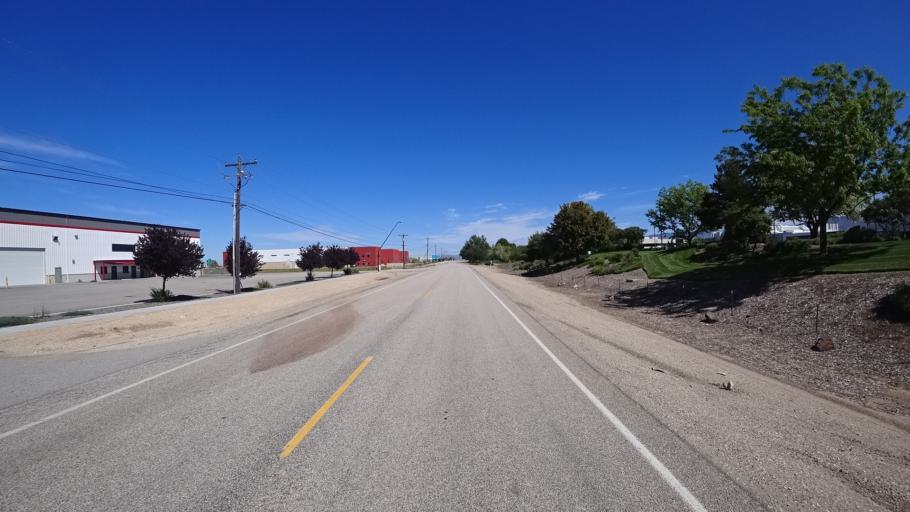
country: US
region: Idaho
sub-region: Ada County
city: Boise
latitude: 43.5228
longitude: -116.1476
